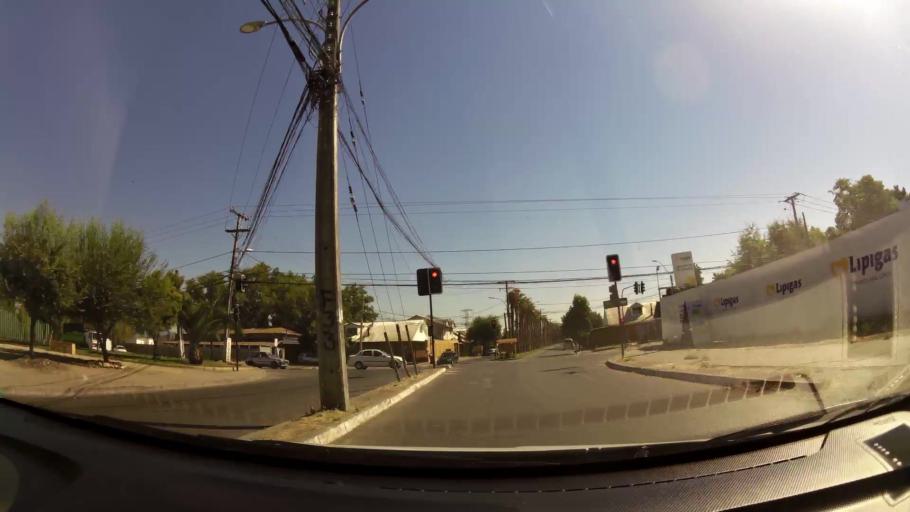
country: CL
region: Maule
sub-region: Provincia de Curico
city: Curico
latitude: -34.9760
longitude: -71.2620
